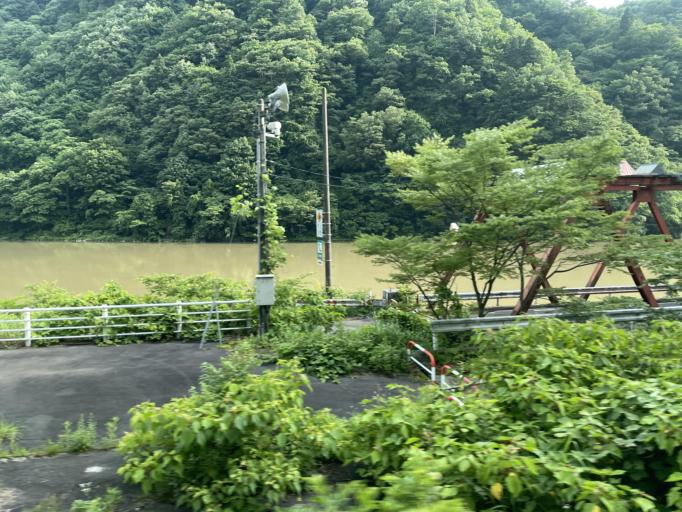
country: JP
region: Niigata
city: Suibara
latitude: 37.6996
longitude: 139.4097
